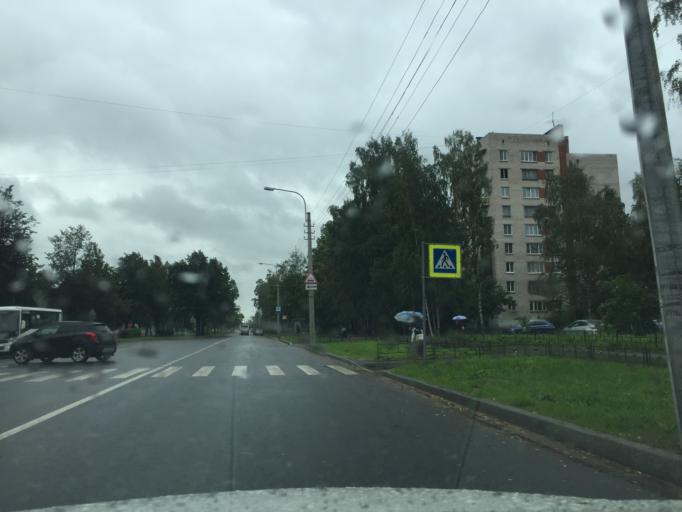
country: RU
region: St.-Petersburg
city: Sosnovaya Polyana
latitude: 59.8308
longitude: 30.1464
